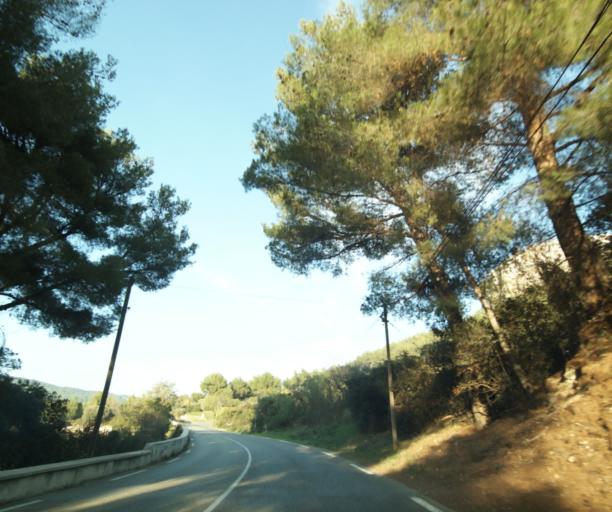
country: FR
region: Provence-Alpes-Cote d'Azur
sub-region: Departement des Bouches-du-Rhone
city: Cassis
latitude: 43.2189
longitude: 5.5668
